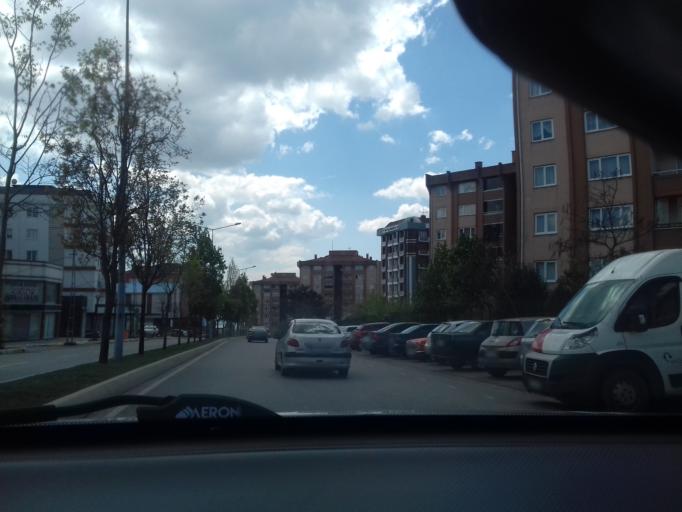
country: TR
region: Istanbul
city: Pendik
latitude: 40.9082
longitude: 29.2786
